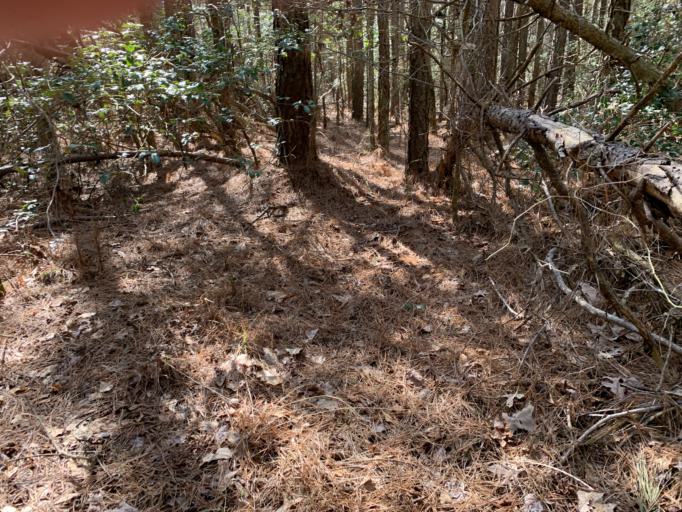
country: US
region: Delaware
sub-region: Sussex County
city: Georgetown
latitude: 38.6811
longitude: -75.4716
